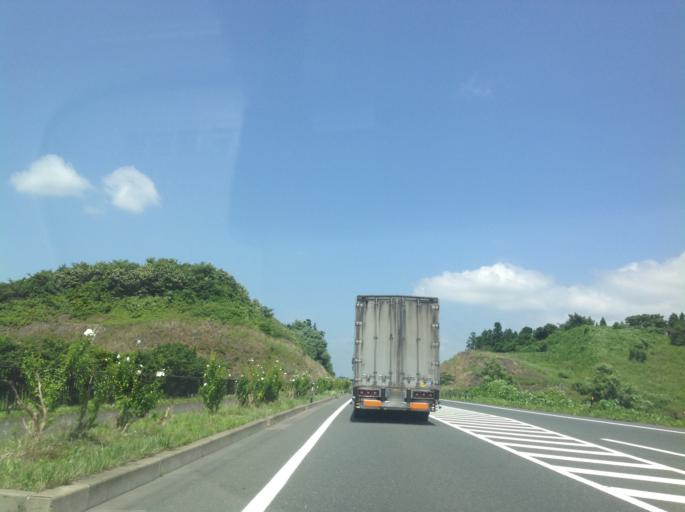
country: JP
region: Iwate
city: Hanamaki
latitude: 39.3813
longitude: 141.1416
